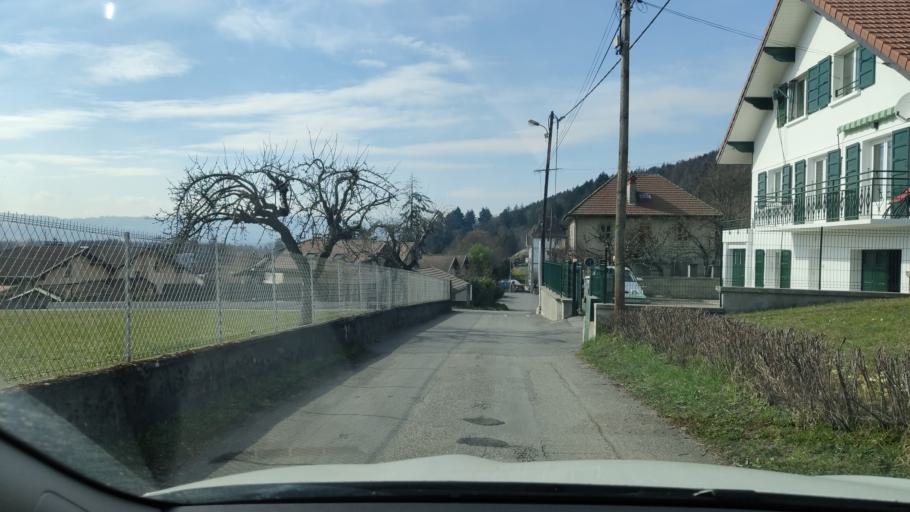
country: FR
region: Rhone-Alpes
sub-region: Departement de la Haute-Savoie
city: Bonneville
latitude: 46.0866
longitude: 6.4057
